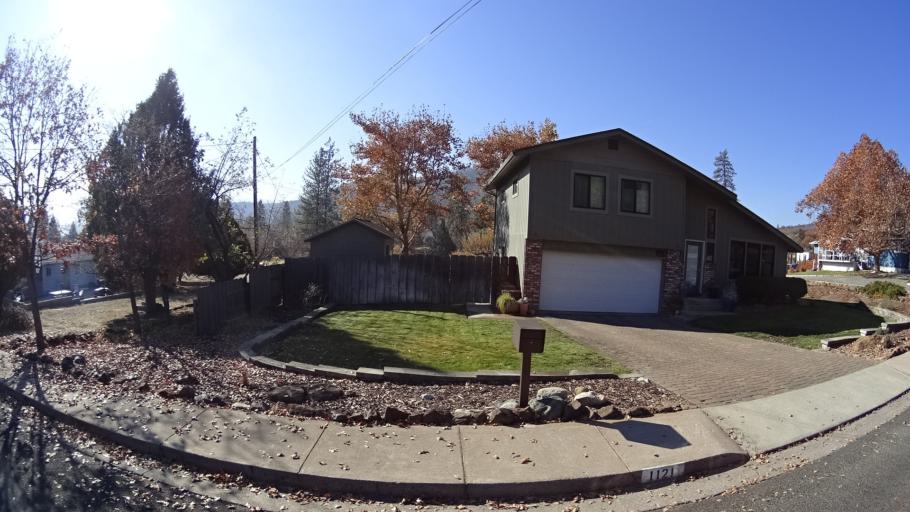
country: US
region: California
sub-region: Siskiyou County
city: Yreka
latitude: 41.7381
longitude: -122.6567
